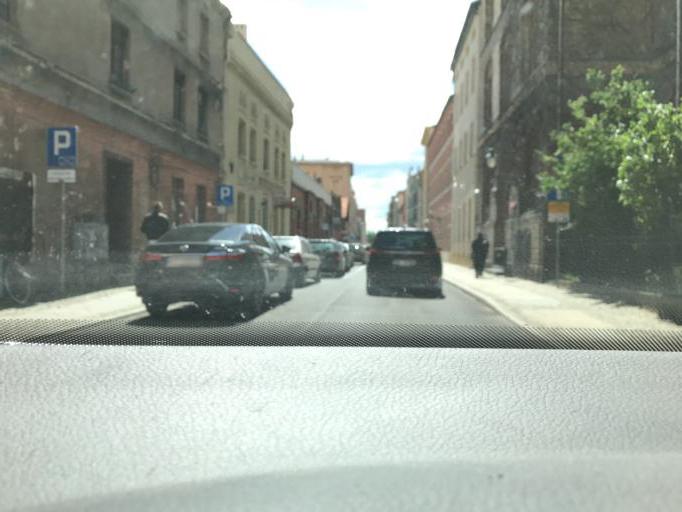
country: PL
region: Kujawsko-Pomorskie
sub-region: Torun
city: Torun
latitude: 53.0112
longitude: 18.6017
